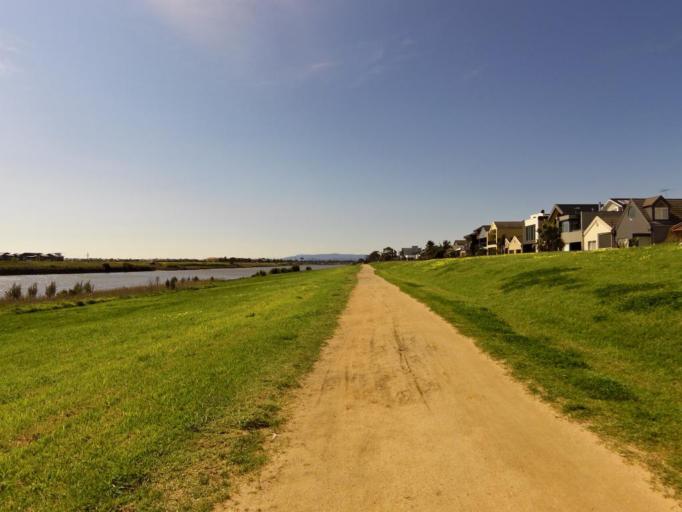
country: AU
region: Victoria
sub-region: Kingston
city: Patterson Lakes
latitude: -38.0674
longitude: 145.1381
